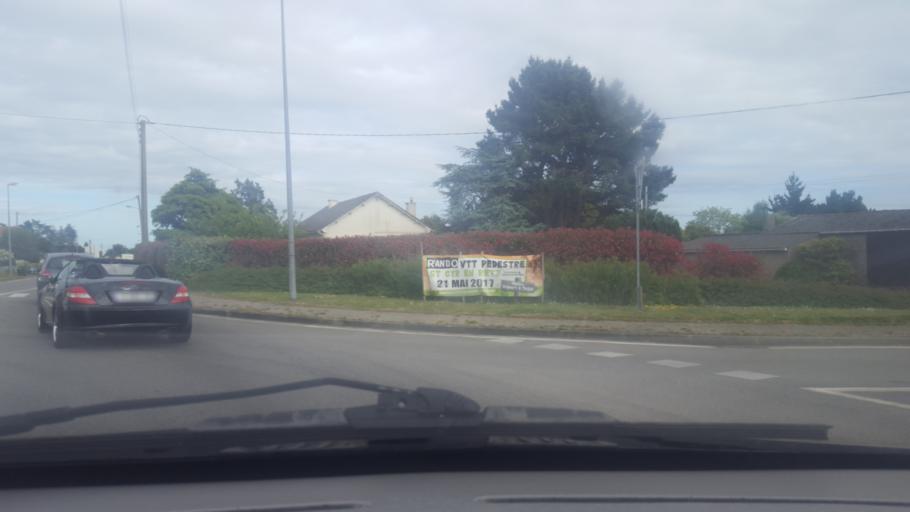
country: FR
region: Pays de la Loire
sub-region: Departement de la Loire-Atlantique
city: Bourgneuf-en-Retz
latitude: 47.0298
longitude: -1.9051
